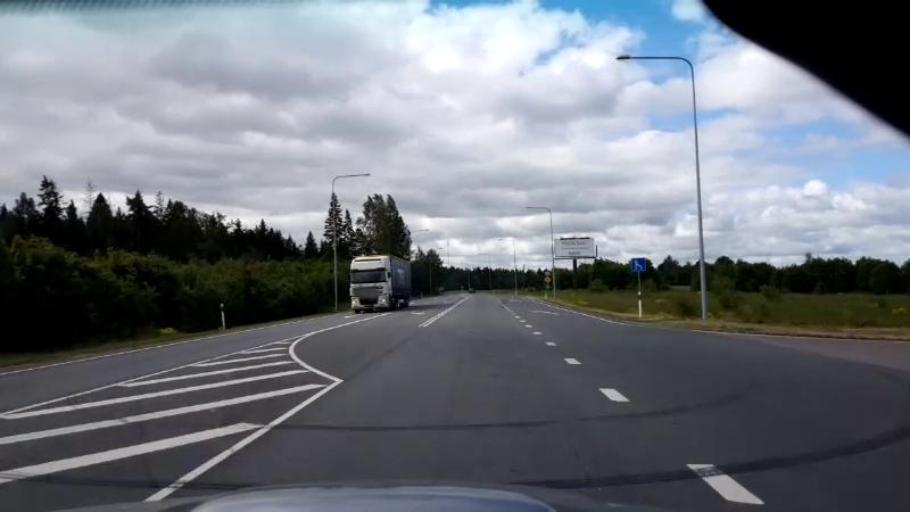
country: EE
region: Raplamaa
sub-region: Maerjamaa vald
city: Marjamaa
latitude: 58.9190
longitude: 24.4573
